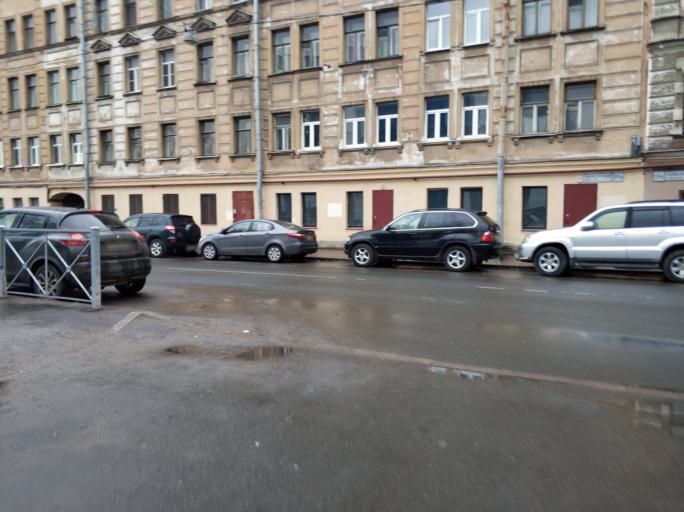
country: RU
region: Leningrad
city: Finlyandskiy
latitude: 59.9675
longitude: 30.3487
